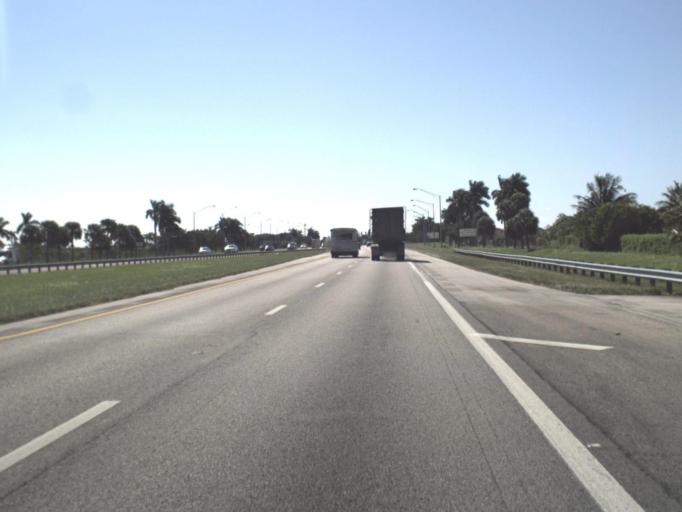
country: US
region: Florida
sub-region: Miami-Dade County
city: Goulds
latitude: 25.5532
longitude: -80.3630
